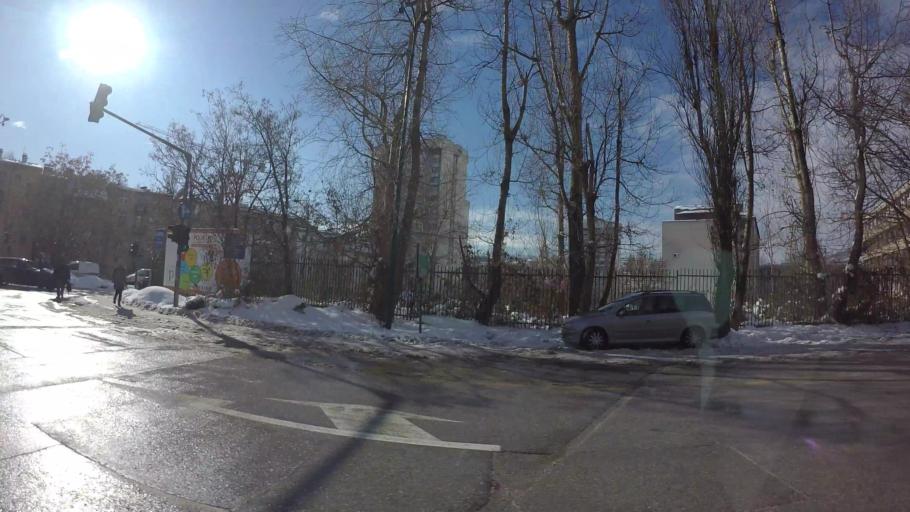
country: BA
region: Federation of Bosnia and Herzegovina
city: Kobilja Glava
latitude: 43.8678
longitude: 18.4149
